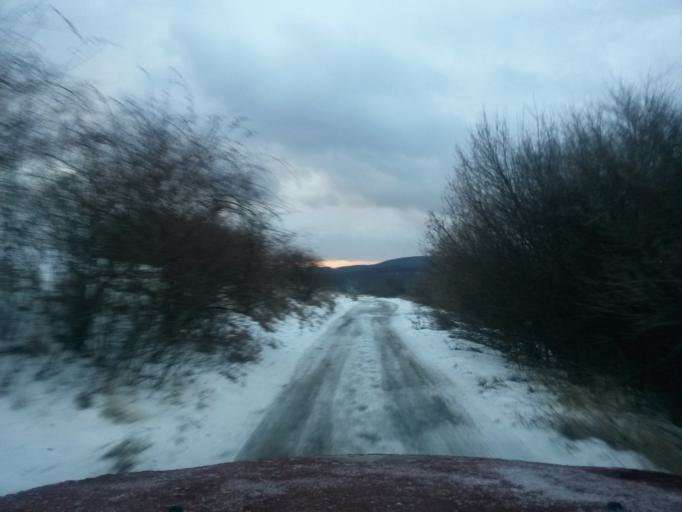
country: SK
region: Kosicky
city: Kosice
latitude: 48.7487
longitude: 21.1222
